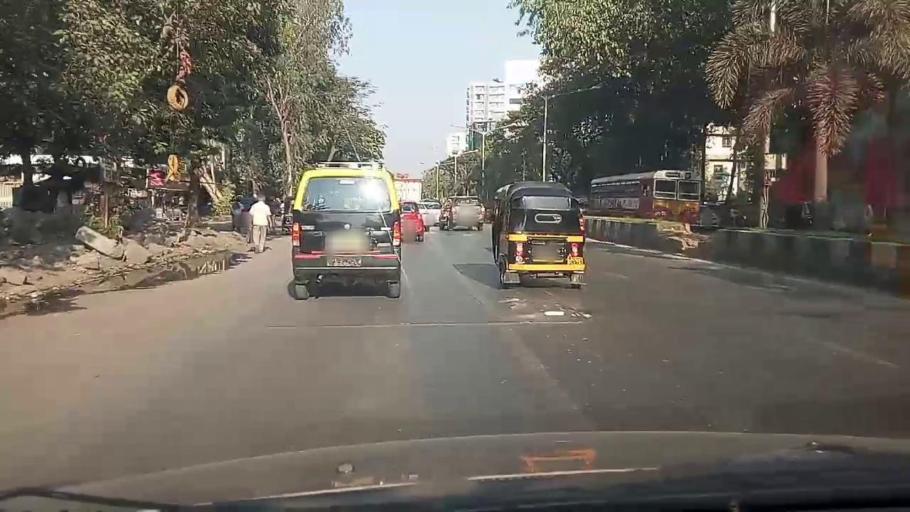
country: IN
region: Maharashtra
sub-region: Mumbai Suburban
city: Mumbai
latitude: 19.0720
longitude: 72.8652
